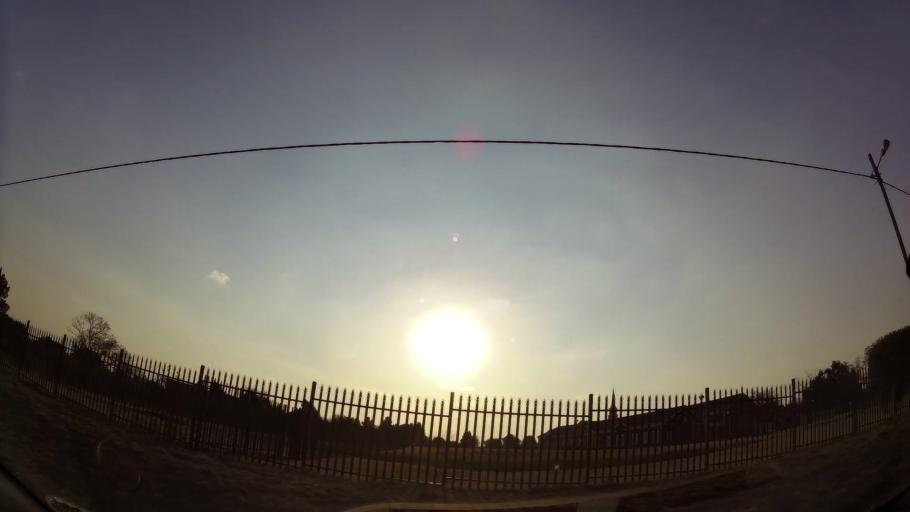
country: ZA
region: Gauteng
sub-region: Ekurhuleni Metropolitan Municipality
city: Benoni
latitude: -26.1523
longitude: 28.3664
